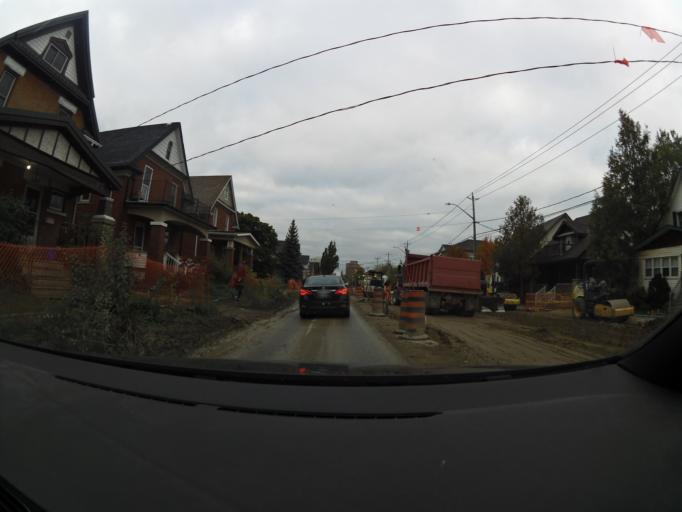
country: CA
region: Ontario
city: Kitchener
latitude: 43.4474
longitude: -80.4776
